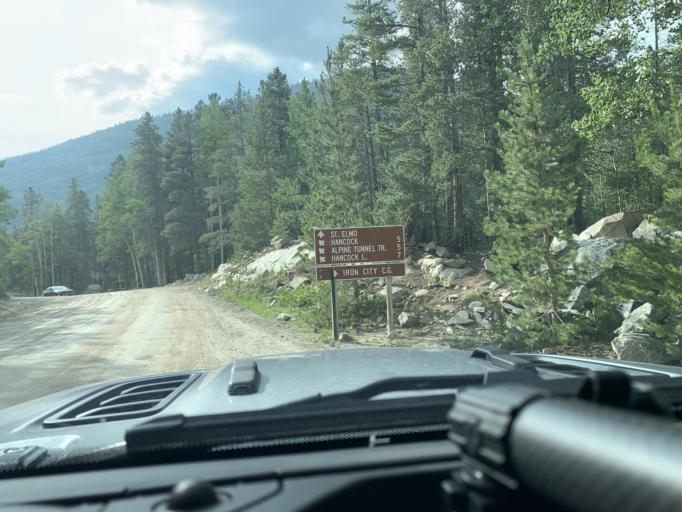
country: US
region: Colorado
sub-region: Chaffee County
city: Buena Vista
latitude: 38.7058
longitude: -106.3395
